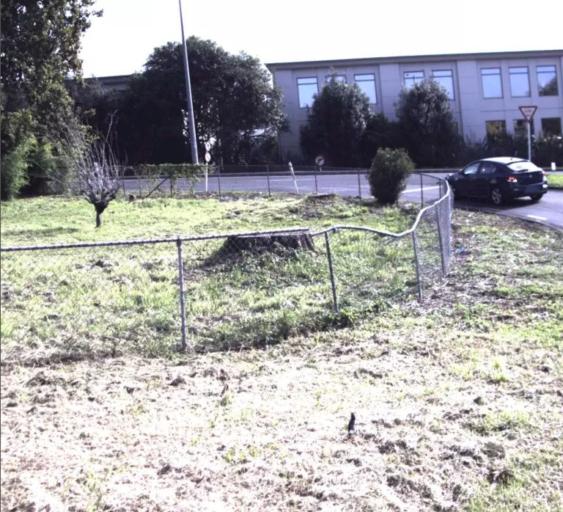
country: NZ
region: Auckland
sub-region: Auckland
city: Tamaki
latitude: -36.9006
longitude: 174.8148
